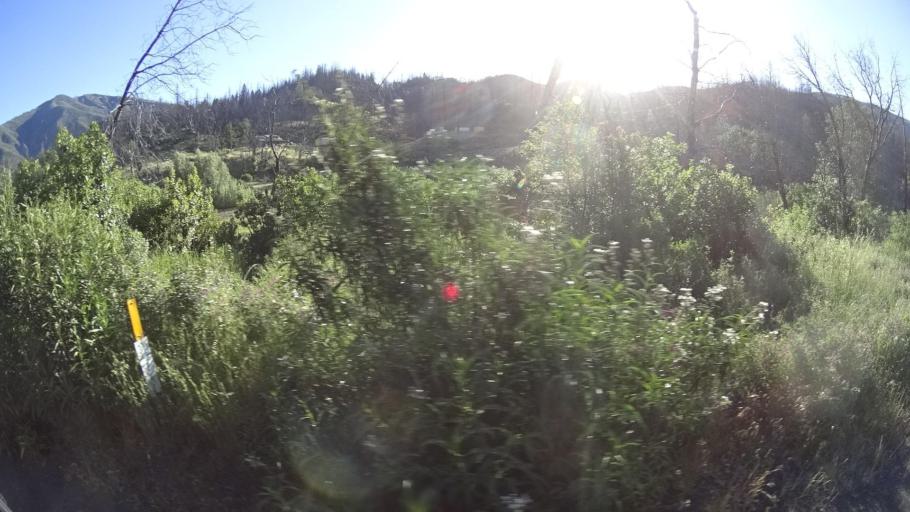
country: US
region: California
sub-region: Lake County
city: Upper Lake
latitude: 39.2445
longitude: -122.9478
